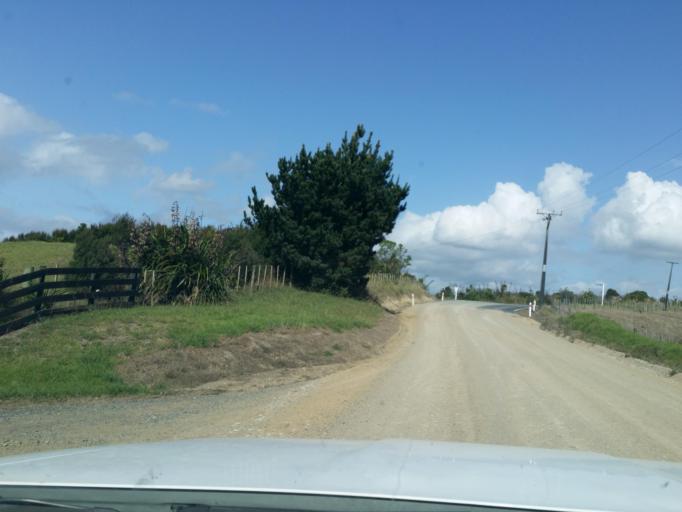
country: NZ
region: Auckland
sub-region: Auckland
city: Wellsford
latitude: -36.1469
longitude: 174.5433
